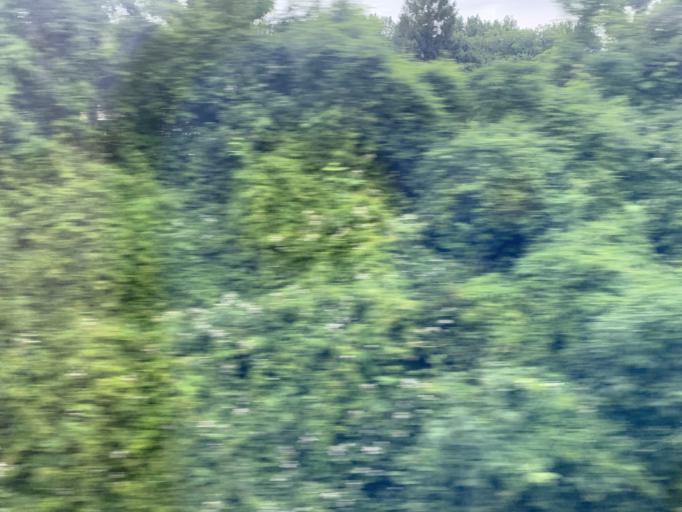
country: FR
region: Alsace
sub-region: Departement du Haut-Rhin
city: Altkirch
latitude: 47.6260
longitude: 7.2522
